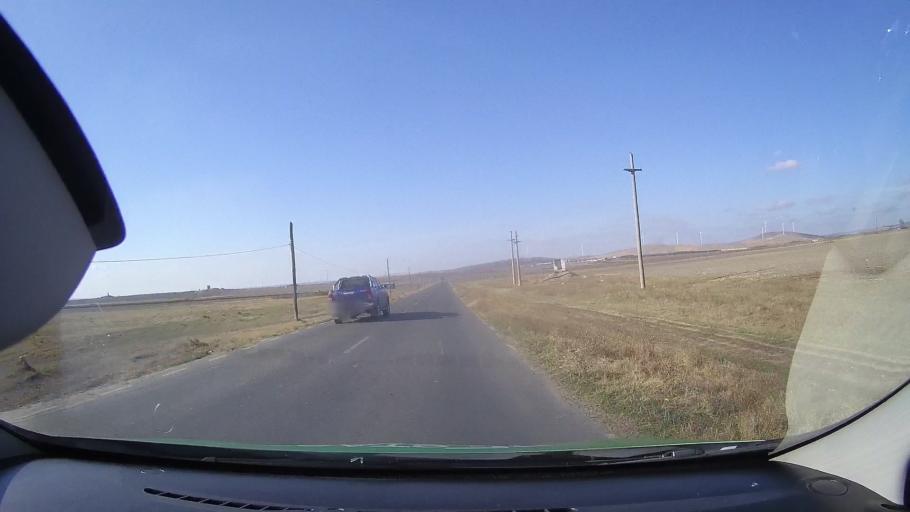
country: RO
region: Tulcea
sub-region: Comuna Ceamurlia de Jos
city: Ceamurlia de Jos
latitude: 44.7476
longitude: 28.7147
